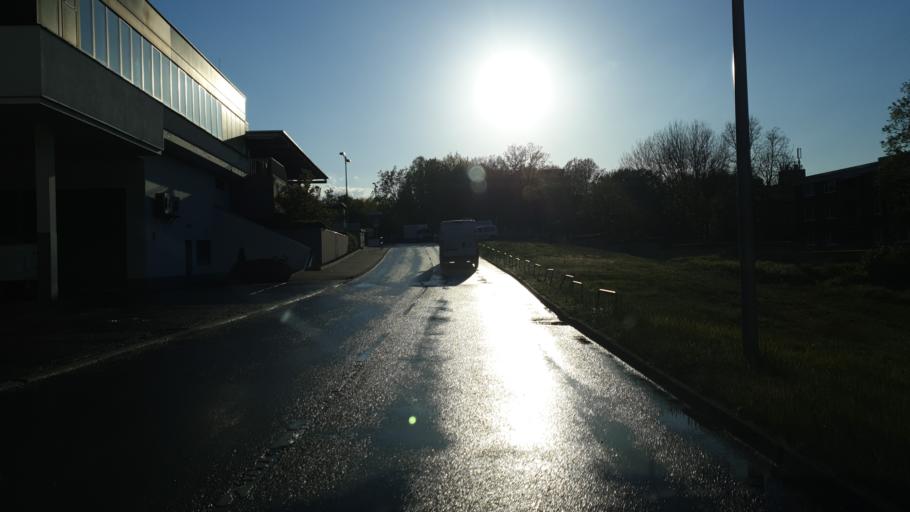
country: DE
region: North Rhine-Westphalia
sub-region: Regierungsbezirk Koln
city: Hurth
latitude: 50.8801
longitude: 6.8743
